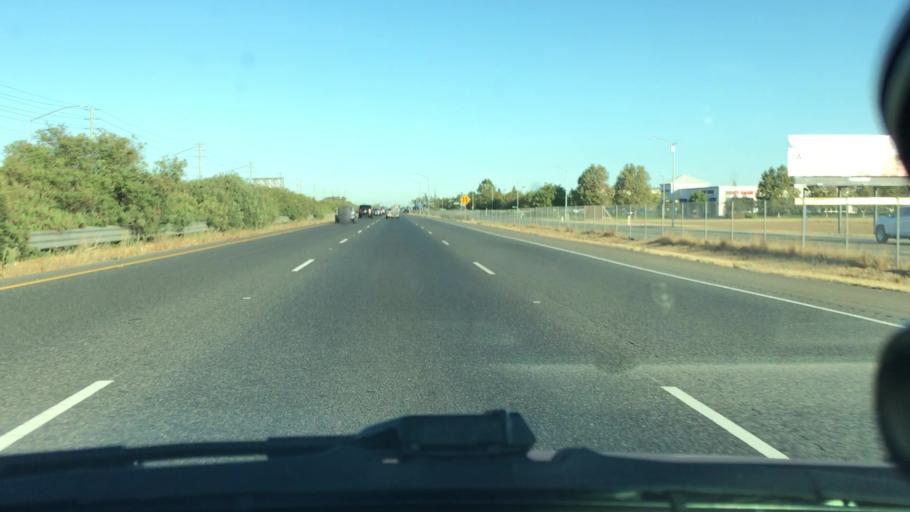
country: US
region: California
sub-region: Sacramento County
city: Elk Grove
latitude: 38.3817
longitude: -121.3671
